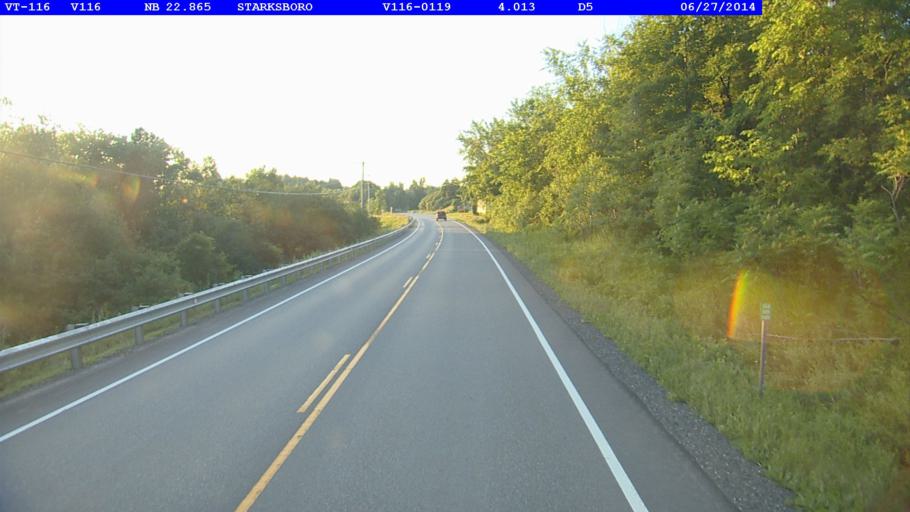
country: US
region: Vermont
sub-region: Chittenden County
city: Hinesburg
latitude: 44.2425
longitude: -73.0585
